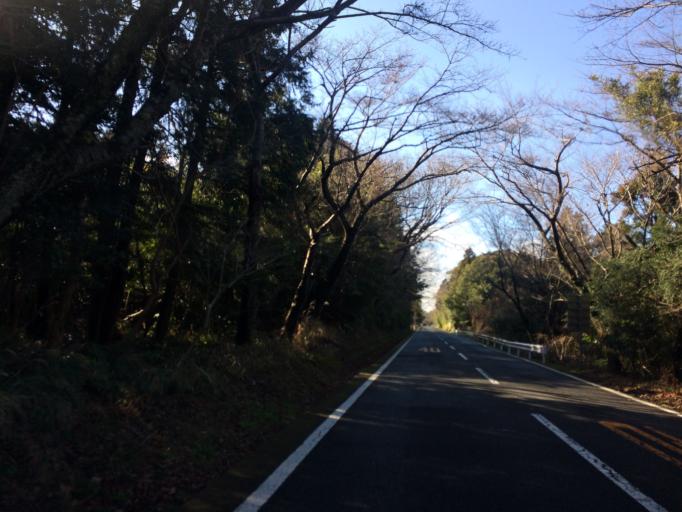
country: JP
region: Shizuoka
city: Shizuoka-shi
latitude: 34.9723
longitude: 138.4485
